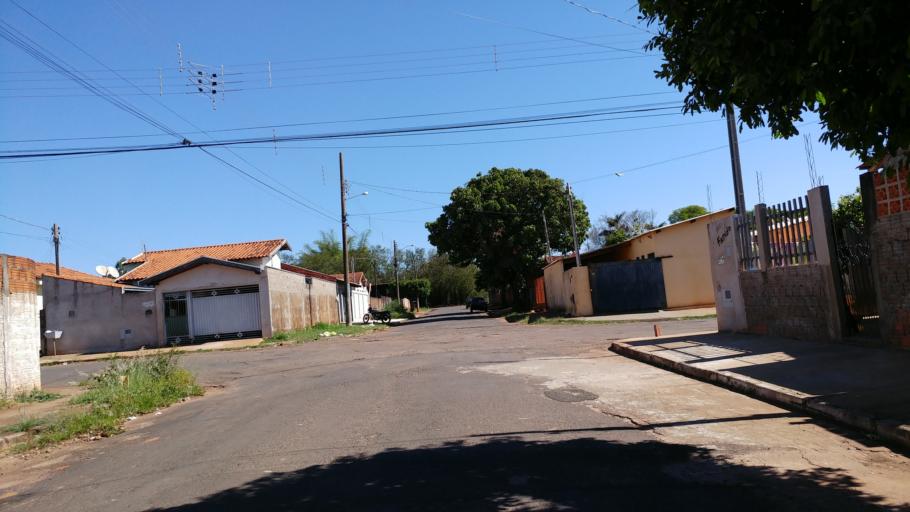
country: BR
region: Sao Paulo
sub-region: Paraguacu Paulista
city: Paraguacu Paulista
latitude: -22.4289
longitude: -50.5870
